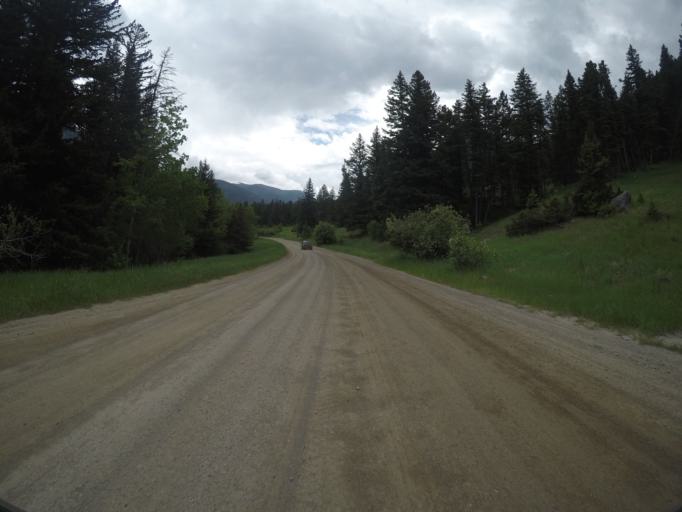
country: US
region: Montana
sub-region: Park County
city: Livingston
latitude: 45.4924
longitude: -110.2254
